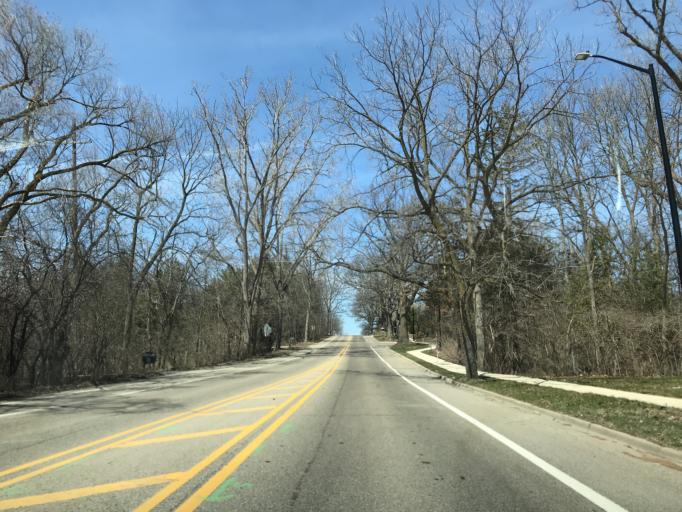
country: US
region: Michigan
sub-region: Washtenaw County
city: Ann Arbor
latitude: 42.3117
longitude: -83.7075
